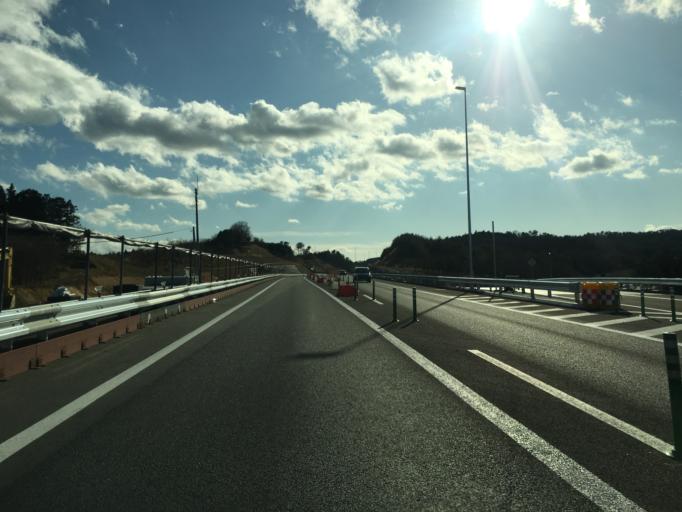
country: JP
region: Fukushima
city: Namie
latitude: 37.4598
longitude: 140.9627
